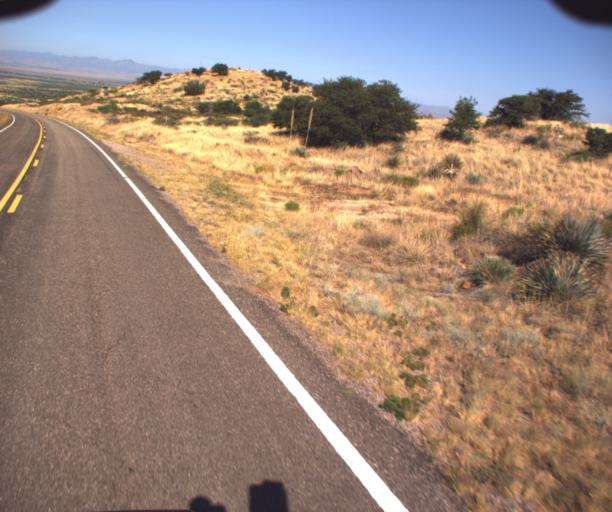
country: US
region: Arizona
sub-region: Graham County
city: Swift Trail Junction
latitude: 32.5998
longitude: -109.8905
